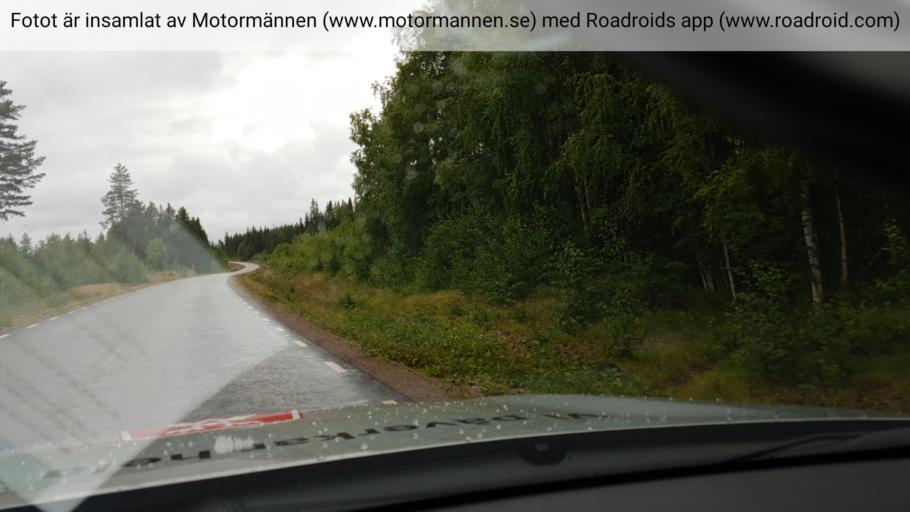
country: SE
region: Norrbotten
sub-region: Gallivare Kommun
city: Gaellivare
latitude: 66.6323
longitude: 20.4073
